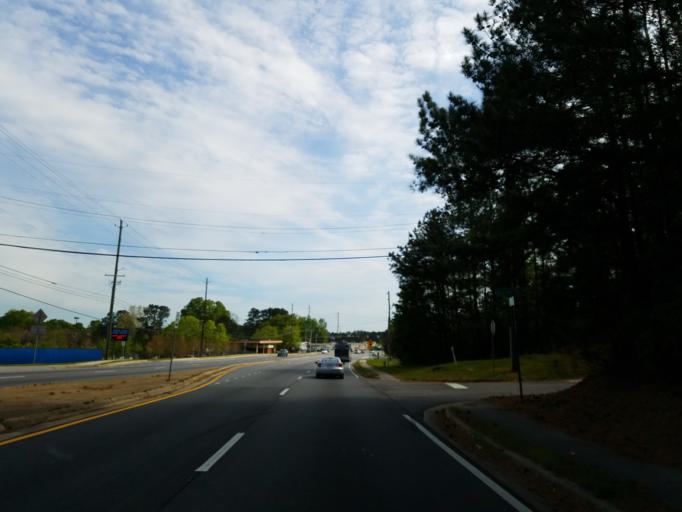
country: US
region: Georgia
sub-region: Cobb County
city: Austell
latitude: 33.8355
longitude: -84.6115
